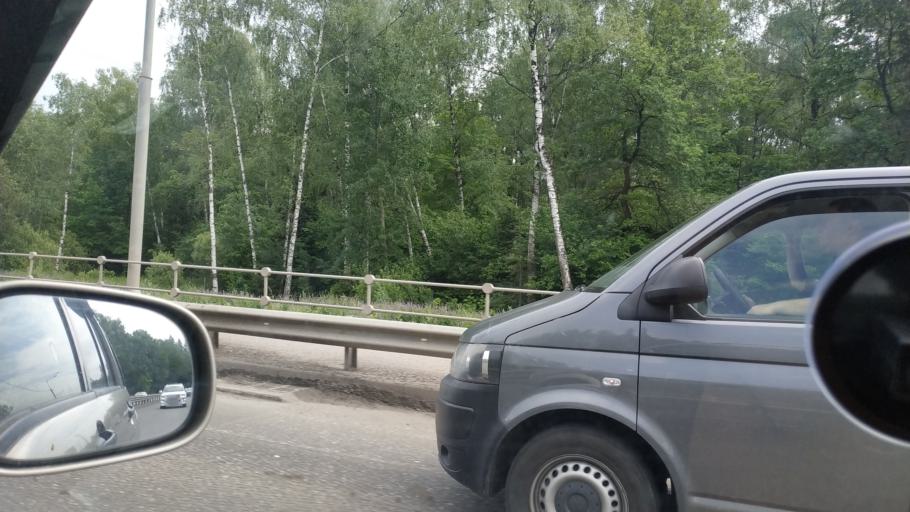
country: RU
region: Moskovskaya
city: Fryazino
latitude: 55.9441
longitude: 38.0390
